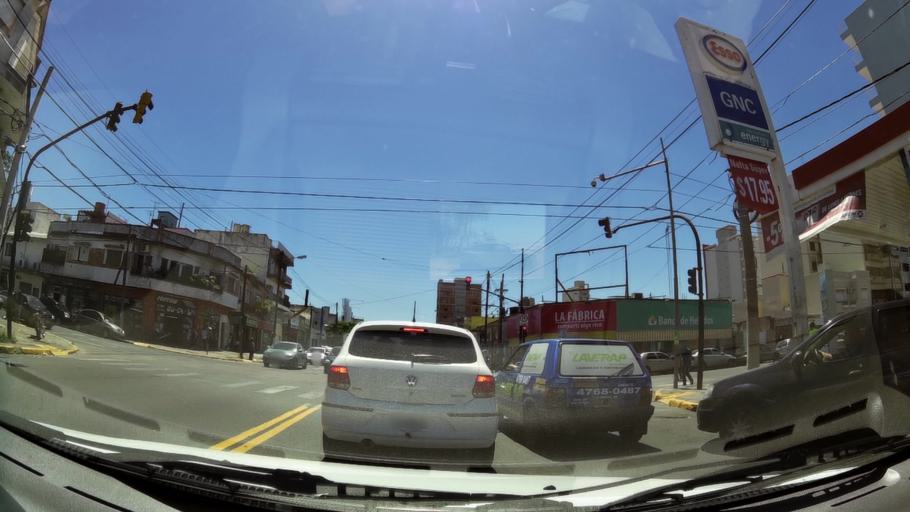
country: AR
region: Buenos Aires
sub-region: Partido de General San Martin
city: General San Martin
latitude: -34.5728
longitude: -58.5441
